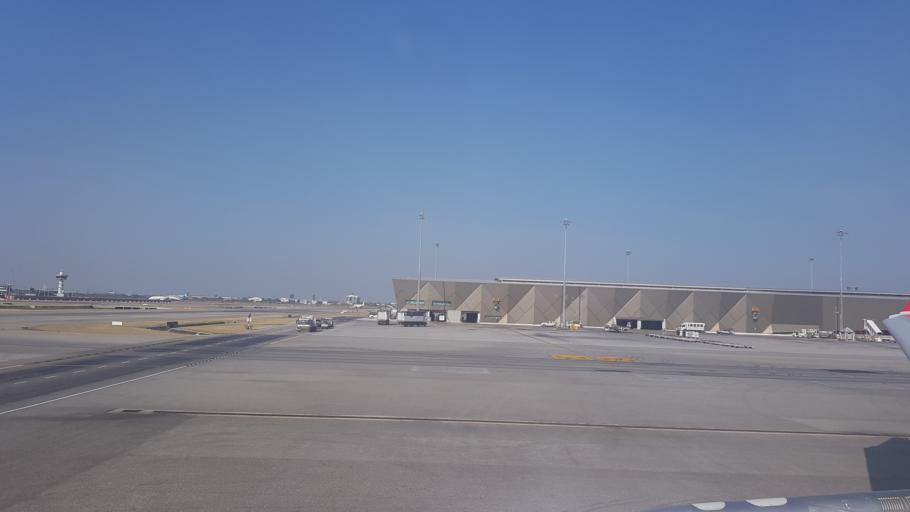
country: TH
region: Bangkok
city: Lat Krabang
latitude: 13.6868
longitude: 100.7515
